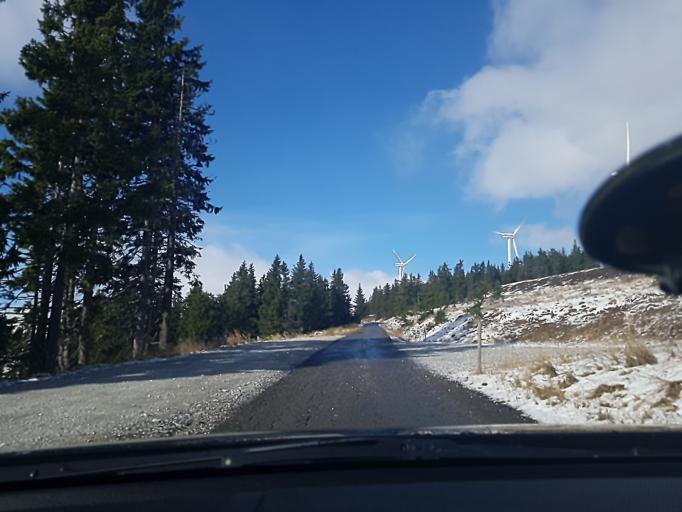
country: AT
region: Styria
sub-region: Politischer Bezirk Murtal
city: Pusterwald
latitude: 47.2729
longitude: 14.4017
